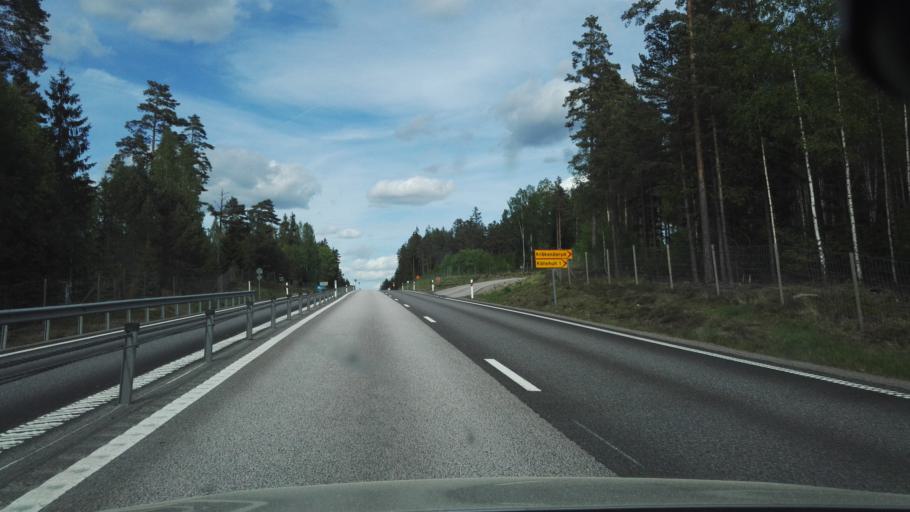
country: SE
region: Kronoberg
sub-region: Vaxjo Kommun
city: Rottne
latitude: 56.9534
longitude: 14.9335
